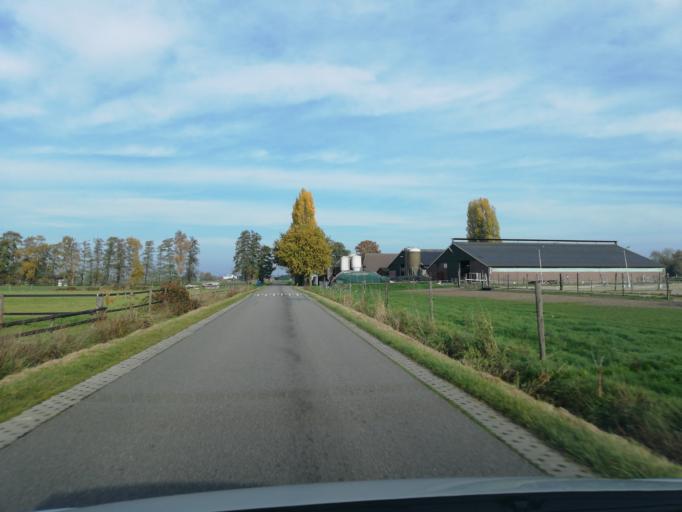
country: NL
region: Gelderland
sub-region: Gemeente Epe
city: Vaassen
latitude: 52.2539
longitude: 6.0166
